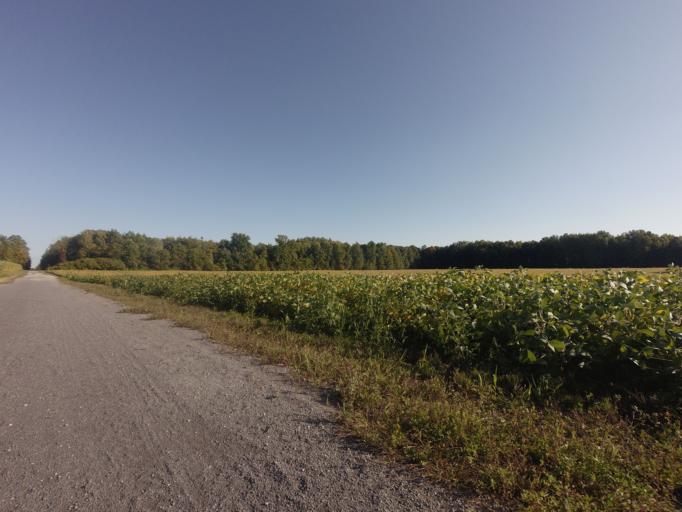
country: CA
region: Ontario
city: Hawkesbury
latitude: 45.5305
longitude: -74.5699
